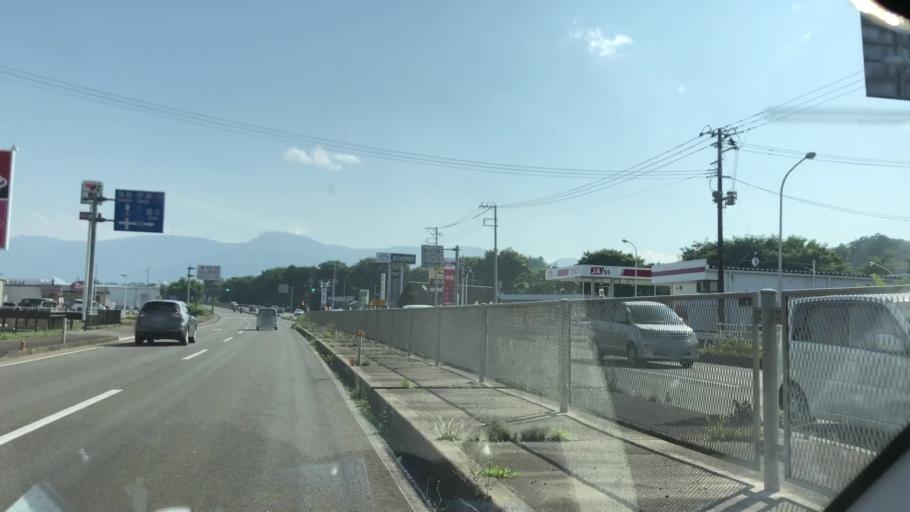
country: JP
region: Miyagi
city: Shiroishi
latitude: 38.0232
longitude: 140.6254
